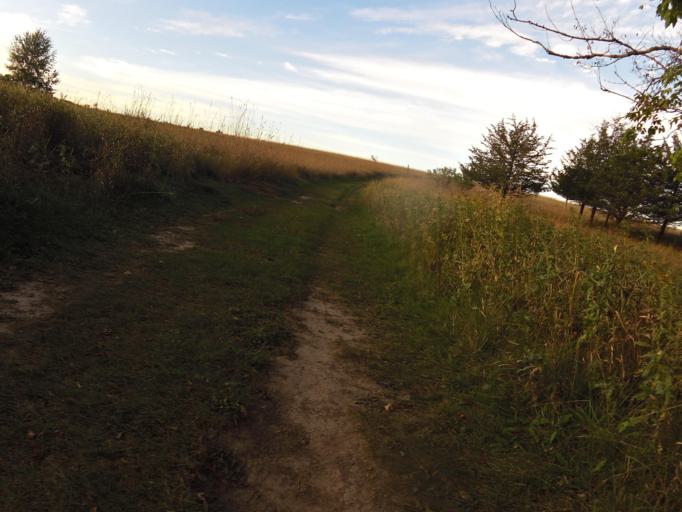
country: US
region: Minnesota
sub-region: Washington County
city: Afton
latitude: 44.8693
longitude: -92.7872
